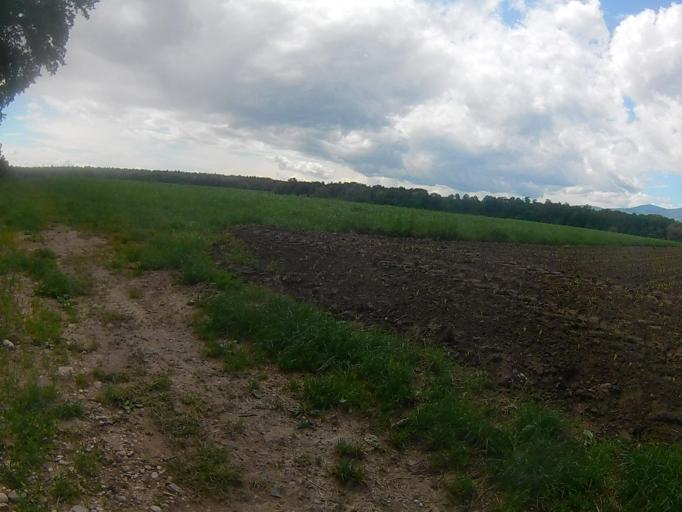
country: SI
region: Duplek
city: Zgornji Duplek
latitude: 46.4964
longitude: 15.7252
